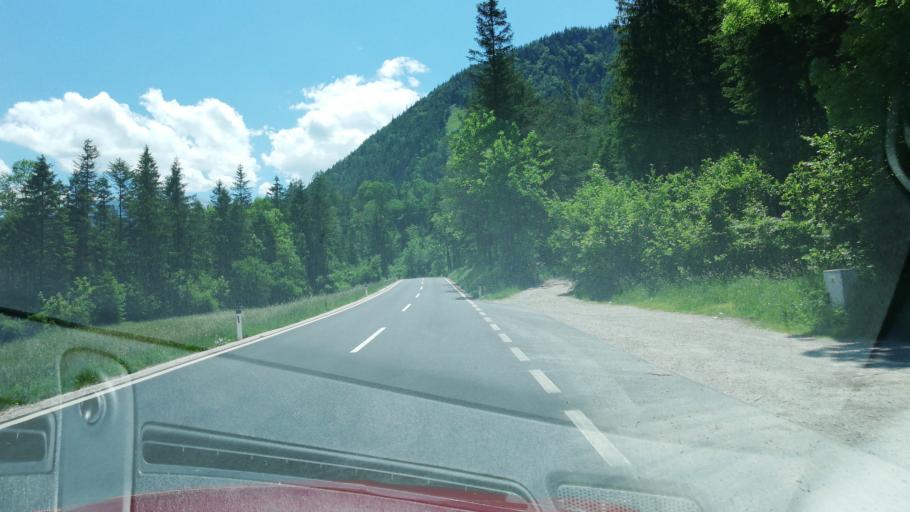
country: AT
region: Upper Austria
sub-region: Politischer Bezirk Kirchdorf an der Krems
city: Rossleithen
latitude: 47.7501
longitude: 14.1622
